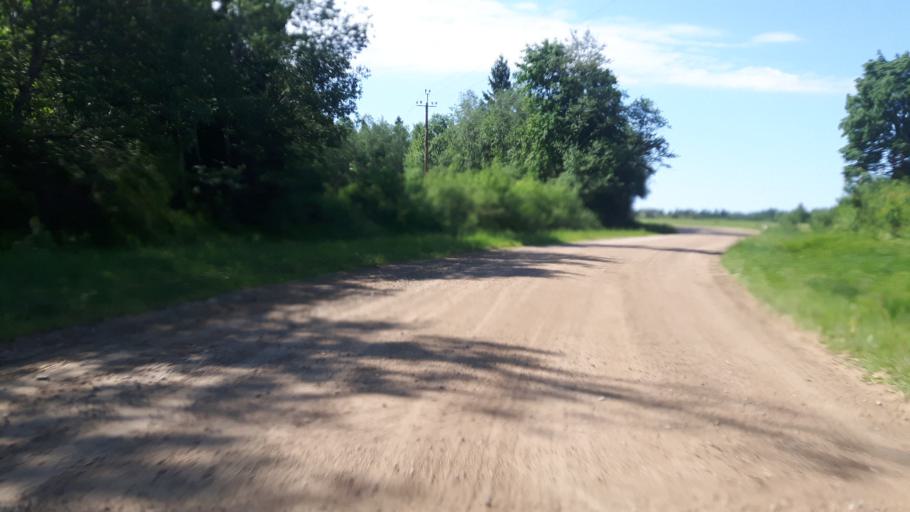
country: EE
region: Paernumaa
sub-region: Vaendra vald (alev)
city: Vandra
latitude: 58.6680
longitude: 25.0273
